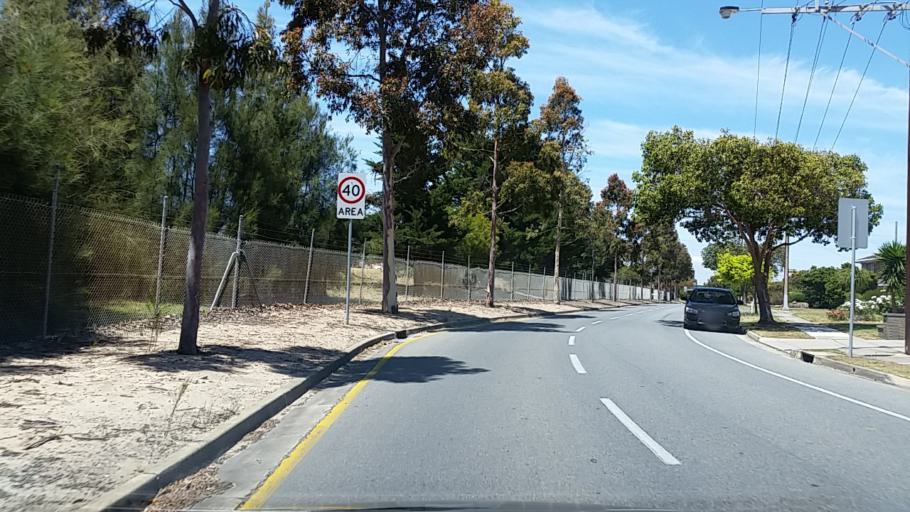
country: AU
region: South Australia
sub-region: Charles Sturt
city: Grange
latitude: -34.8901
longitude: 138.5018
